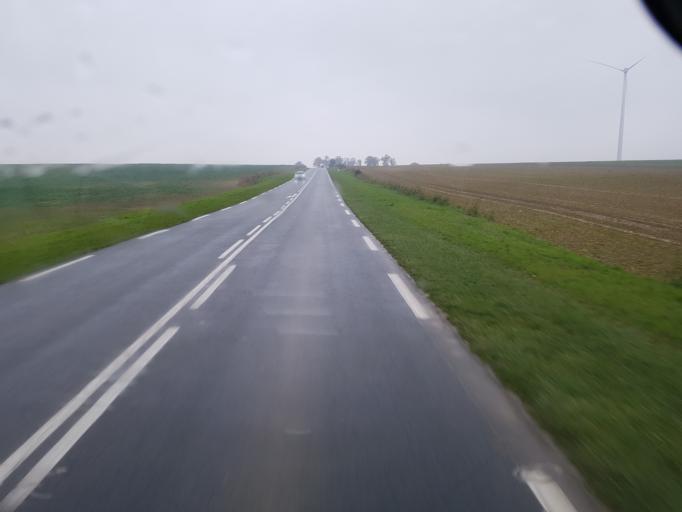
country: FR
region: Picardie
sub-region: Departement de l'Aisne
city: Omissy
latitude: 49.9012
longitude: 3.2616
